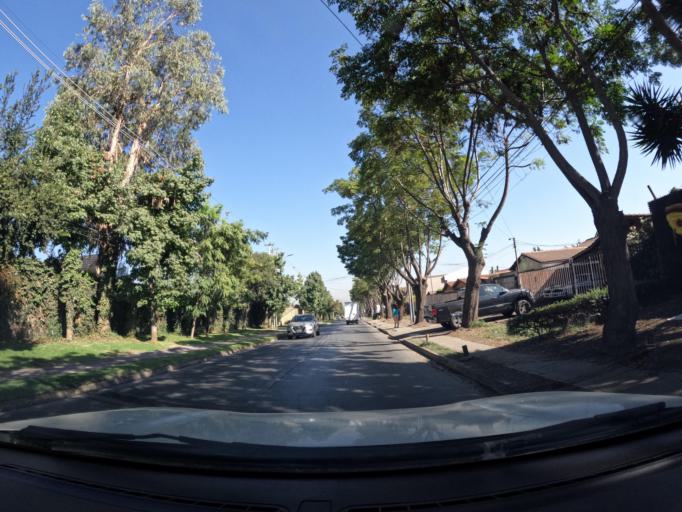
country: CL
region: Santiago Metropolitan
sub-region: Provincia de Santiago
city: Villa Presidente Frei, Nunoa, Santiago, Chile
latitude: -33.4808
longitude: -70.5414
